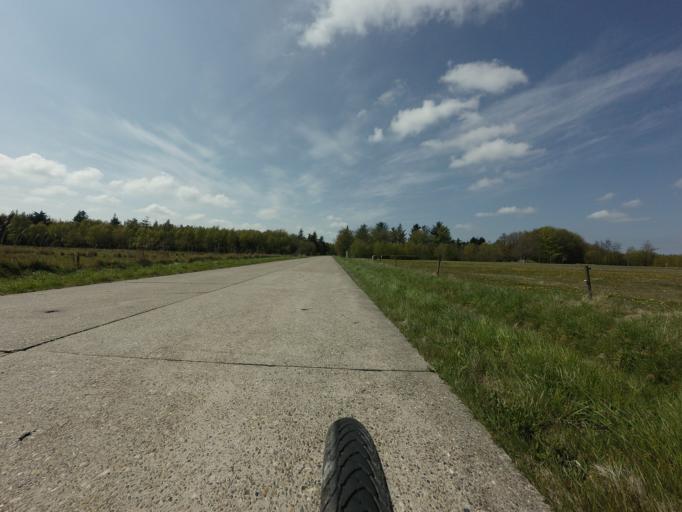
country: DK
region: North Denmark
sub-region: Jammerbugt Kommune
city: Brovst
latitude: 57.1644
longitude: 9.4885
